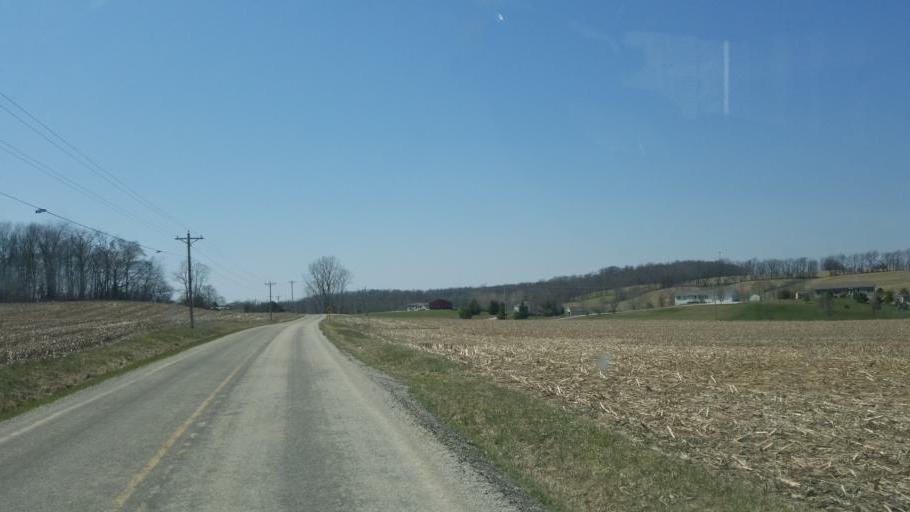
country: US
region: Ohio
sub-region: Ashland County
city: Loudonville
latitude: 40.7513
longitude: -82.2386
